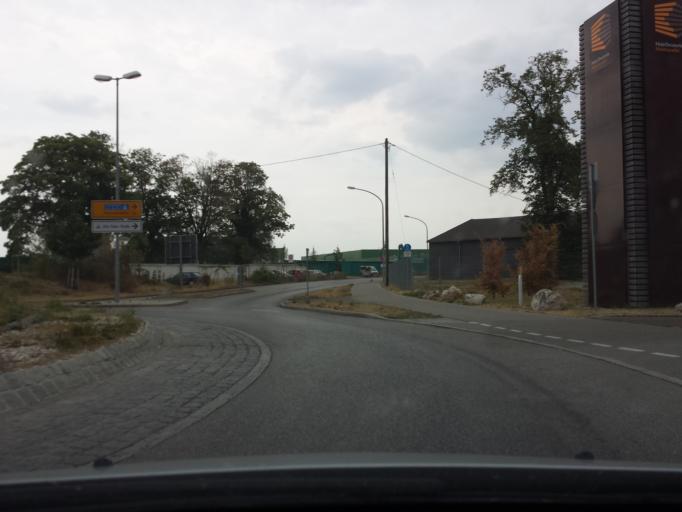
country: DE
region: Bavaria
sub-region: Swabia
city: Neu-Ulm
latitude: 48.3976
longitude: 10.0284
